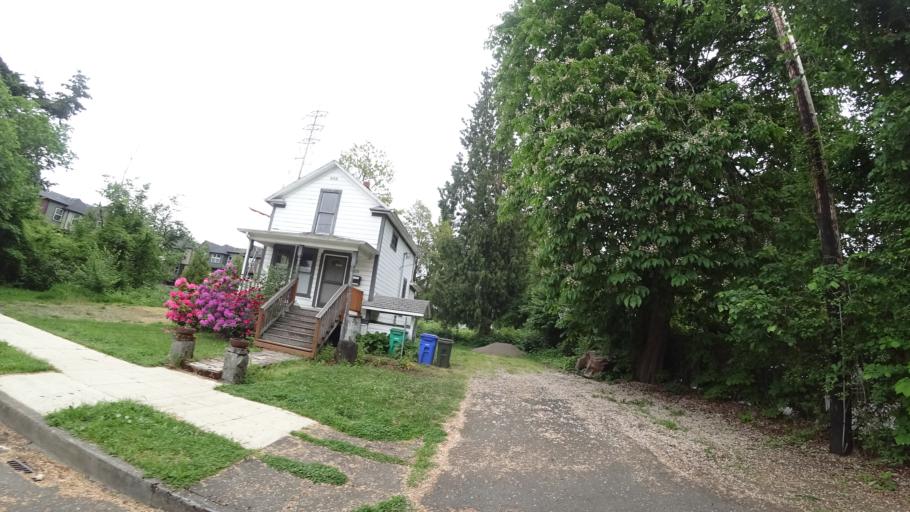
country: US
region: Oregon
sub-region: Clackamas County
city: Milwaukie
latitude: 45.4582
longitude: -122.6550
